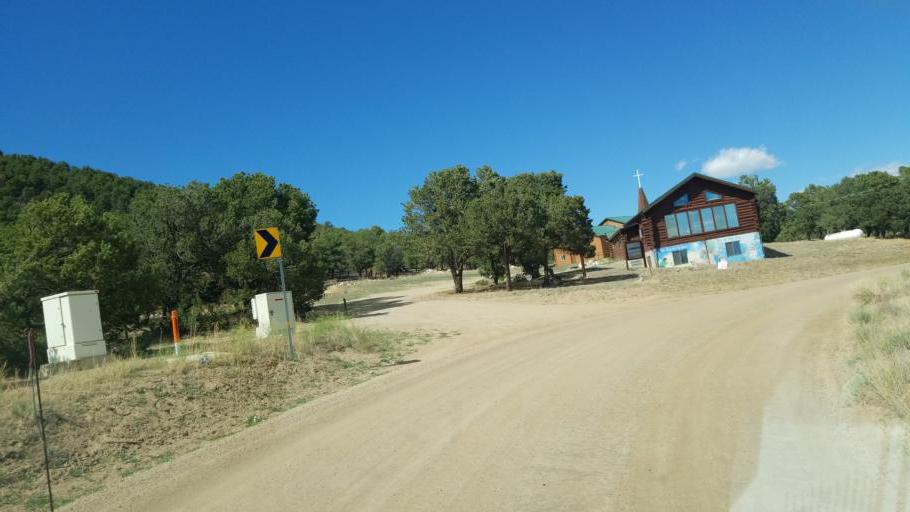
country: US
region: Colorado
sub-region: Custer County
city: Westcliffe
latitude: 38.2977
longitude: -105.4911
